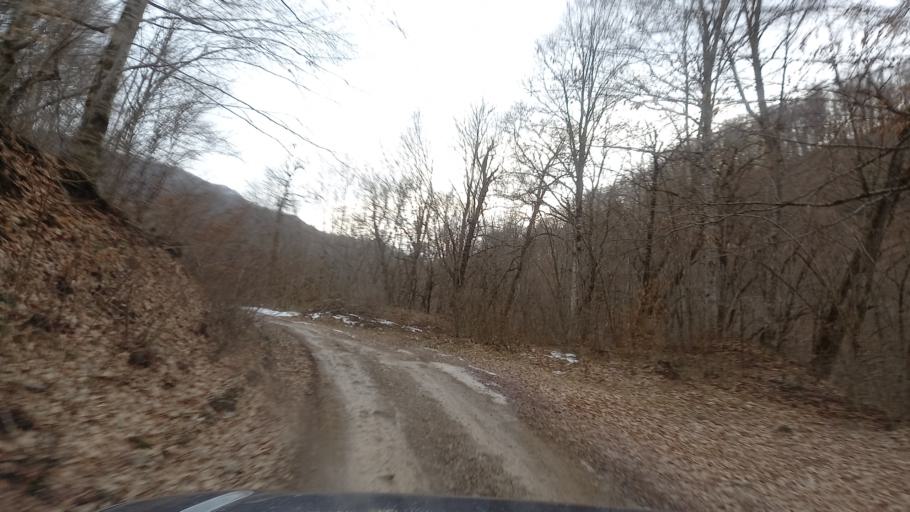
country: RU
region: Adygeya
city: Kamennomostskiy
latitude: 44.1589
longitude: 40.2985
